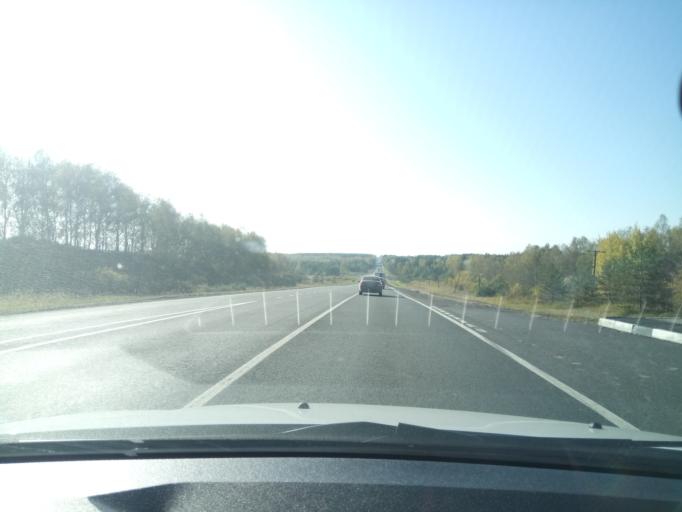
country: RU
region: Nizjnij Novgorod
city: Dal'neye Konstantinovo
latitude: 55.9640
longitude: 43.9748
